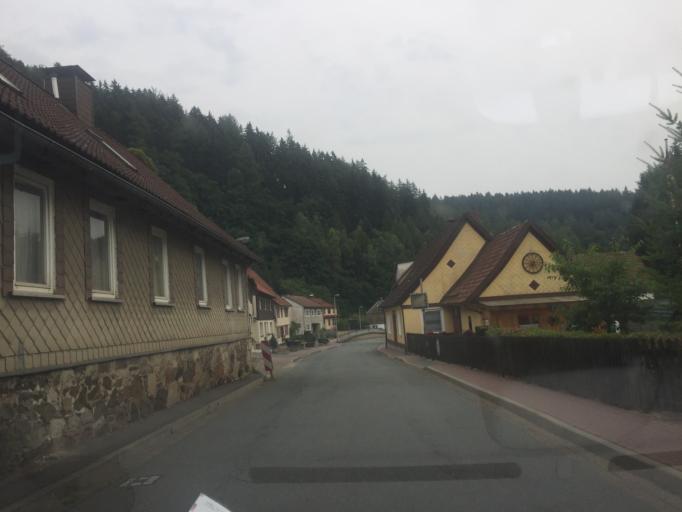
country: DE
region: Lower Saxony
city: Wieda
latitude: 51.6394
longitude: 10.5886
